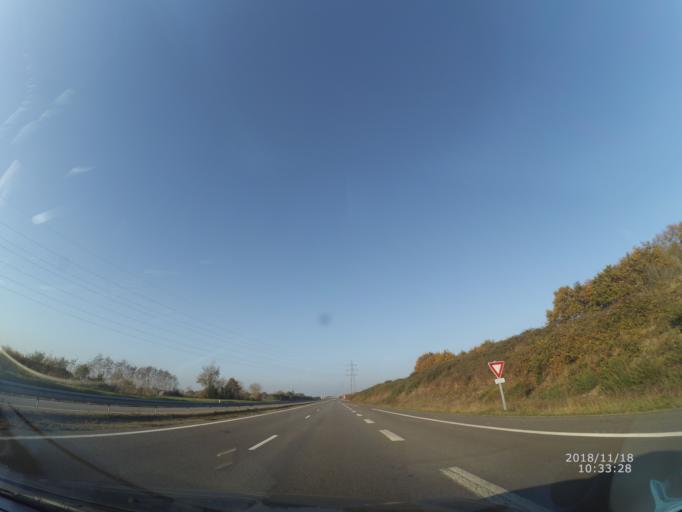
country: FR
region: Pays de la Loire
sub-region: Departement de la Loire-Atlantique
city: Saint-Jean-de-Boiseau
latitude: 47.1848
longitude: -1.7312
